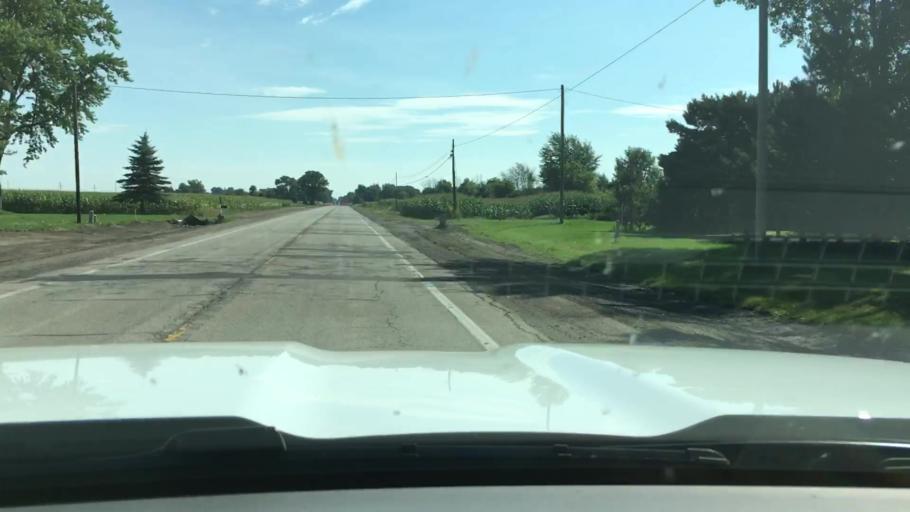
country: US
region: Michigan
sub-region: Saginaw County
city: Hemlock
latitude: 43.4122
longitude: -84.2824
